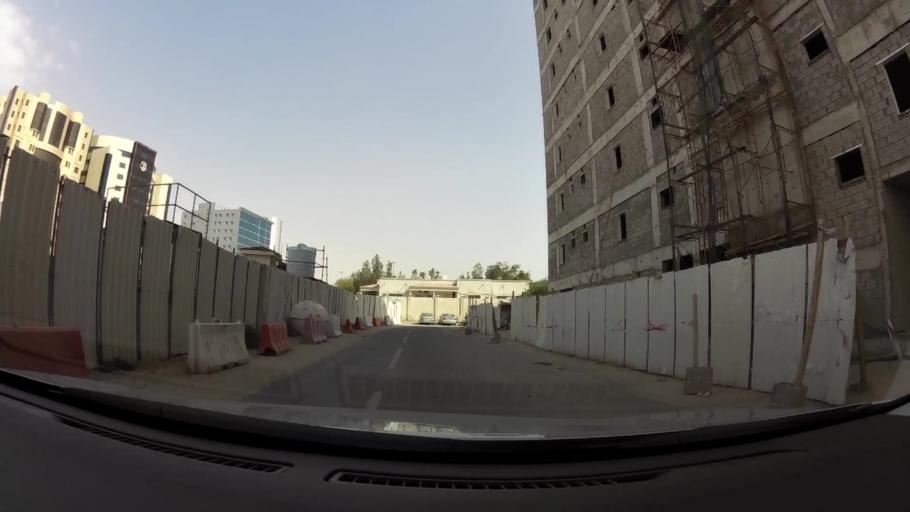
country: QA
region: Baladiyat ad Dawhah
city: Doha
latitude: 25.2881
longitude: 51.5068
